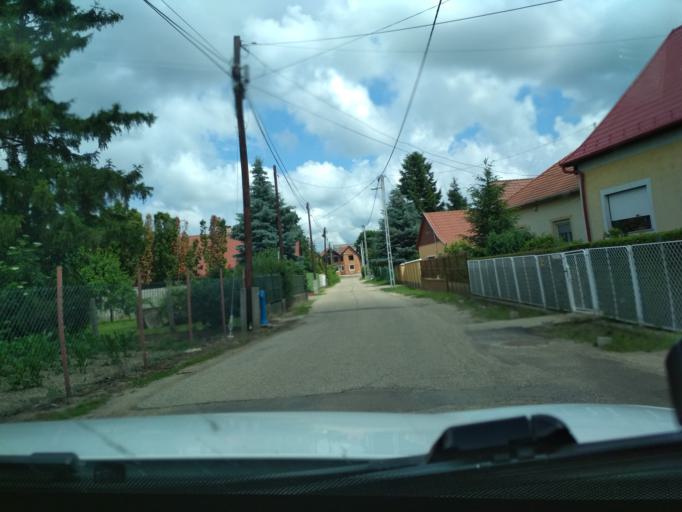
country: HU
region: Jasz-Nagykun-Szolnok
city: Tiszafured
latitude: 47.6174
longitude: 20.7420
